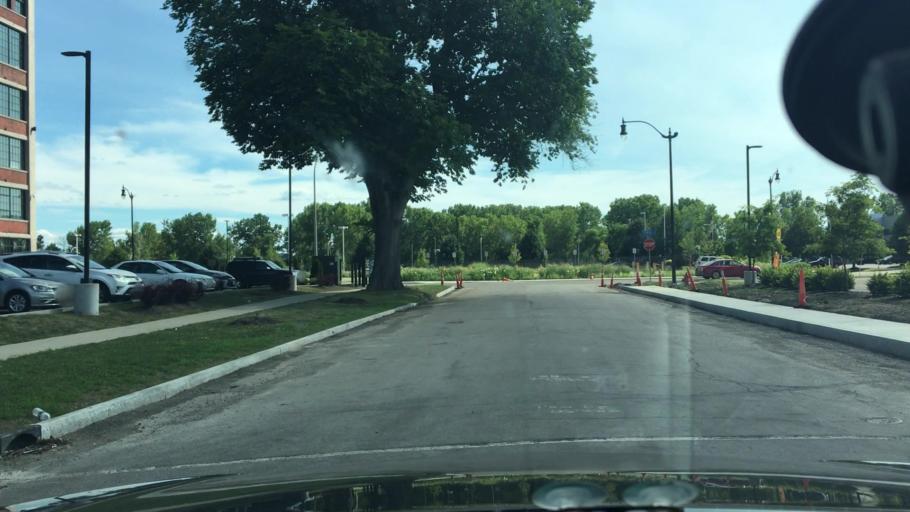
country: US
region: New York
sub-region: Erie County
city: Buffalo
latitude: 42.8781
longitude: -78.8580
